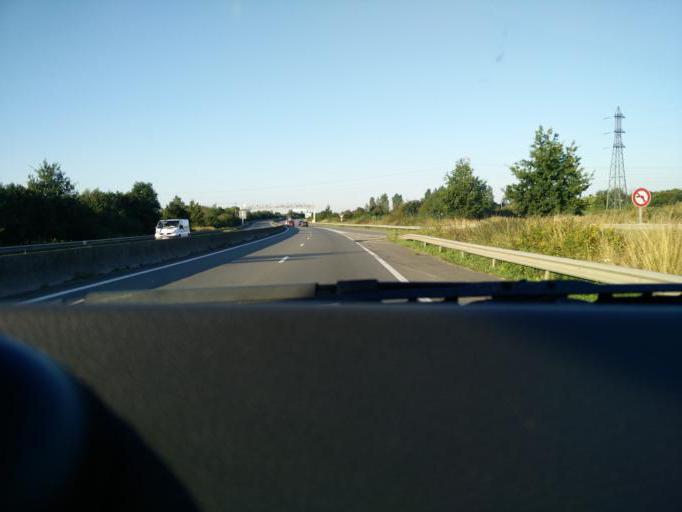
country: FR
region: Nord-Pas-de-Calais
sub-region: Departement du Nord
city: Santes
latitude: 50.6017
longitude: 2.9420
